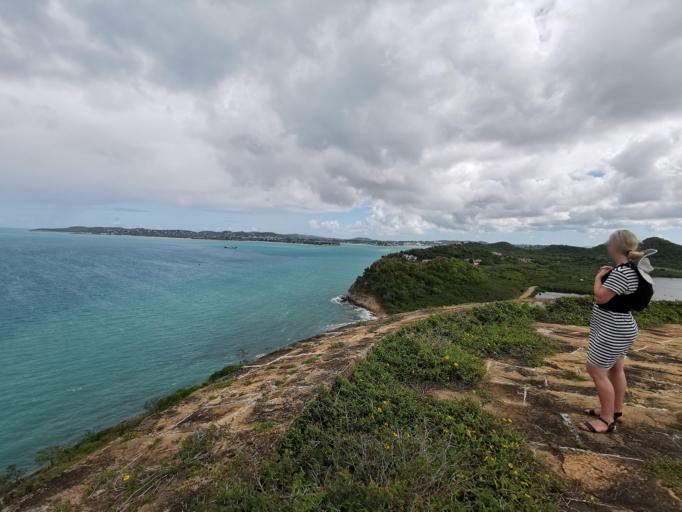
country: AG
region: Saint John
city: Saint John's
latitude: 17.1244
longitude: -61.8855
